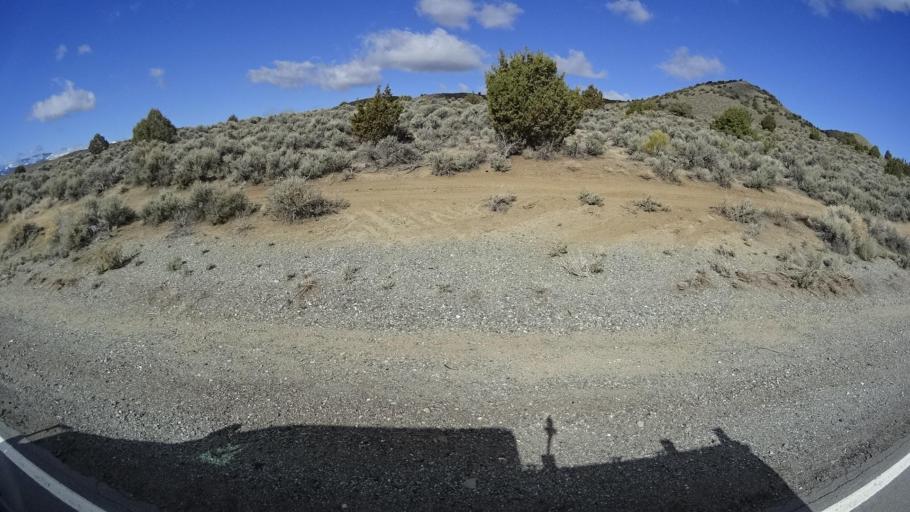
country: US
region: Nevada
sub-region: Washoe County
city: Cold Springs
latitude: 39.7038
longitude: -119.9075
